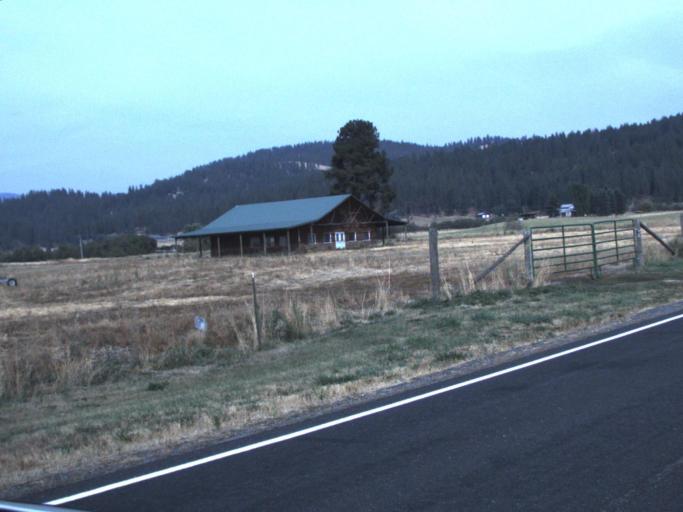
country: US
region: Washington
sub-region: Spokane County
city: Trentwood
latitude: 47.8022
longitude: -117.2215
